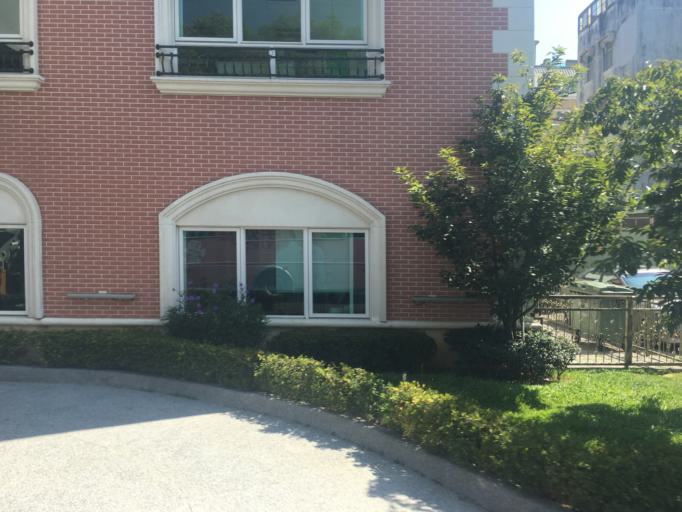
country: TW
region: Taiwan
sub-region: Hsinchu
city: Hsinchu
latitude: 24.7987
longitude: 120.9830
